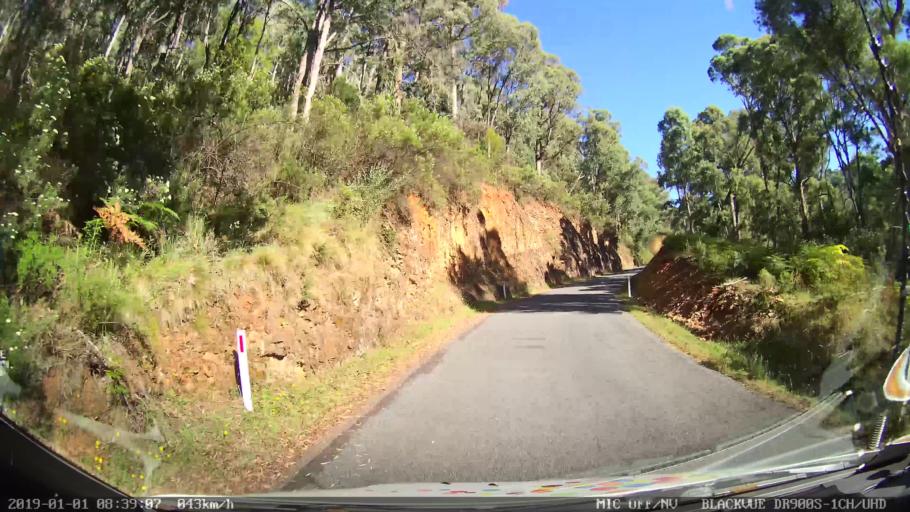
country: AU
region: New South Wales
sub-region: Snowy River
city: Jindabyne
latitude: -36.3334
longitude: 148.1936
